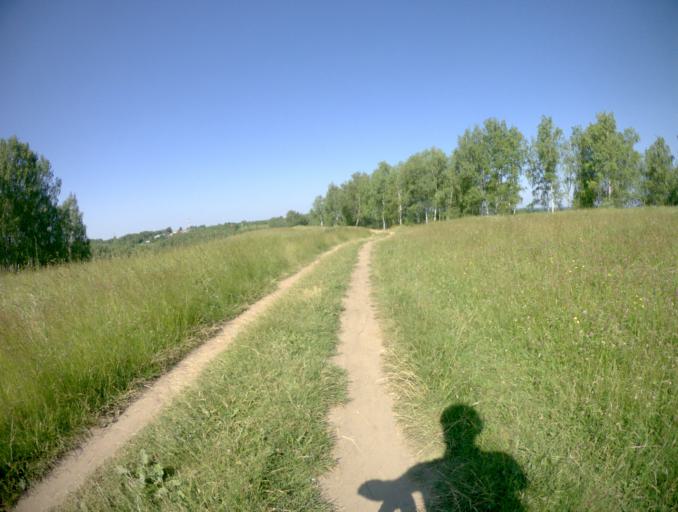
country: RU
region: Vladimir
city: Novovyazniki
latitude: 56.2362
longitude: 42.2439
